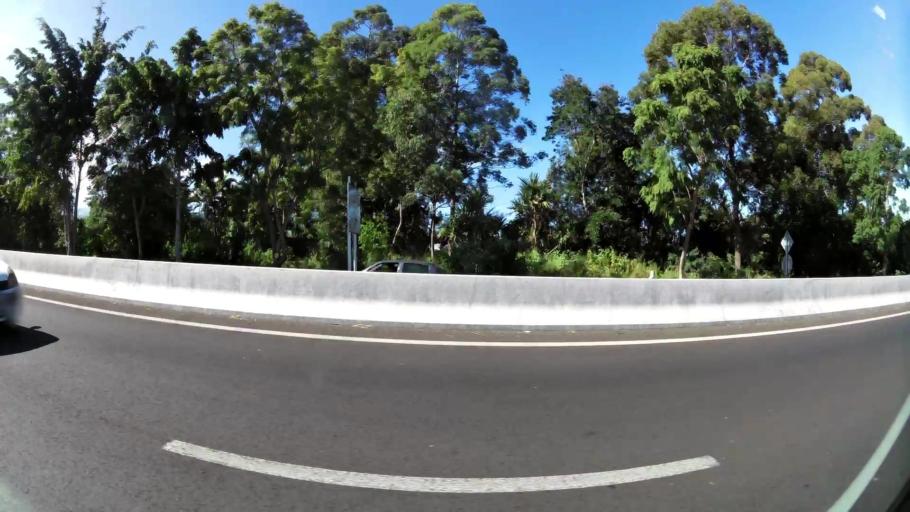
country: RE
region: Reunion
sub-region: Reunion
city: Le Tampon
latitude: -21.2879
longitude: 55.5152
